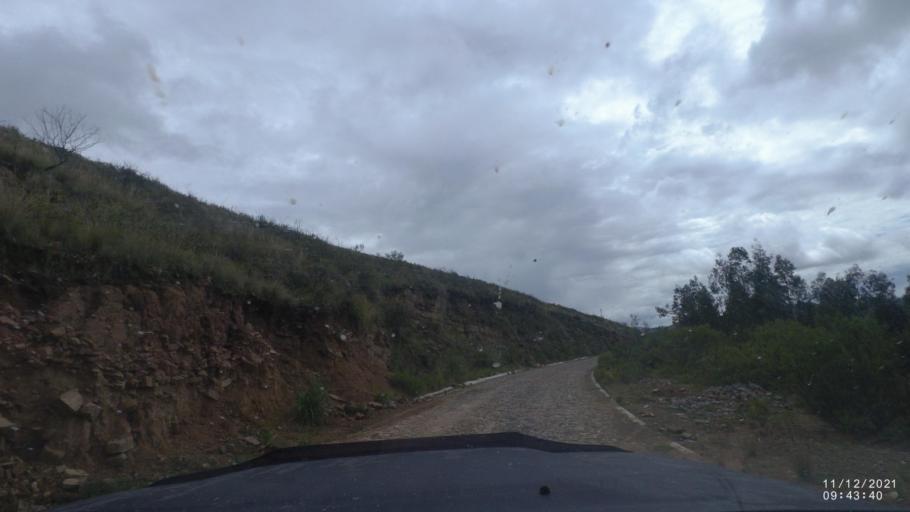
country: BO
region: Cochabamba
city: Tarata
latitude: -17.7997
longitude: -65.9776
